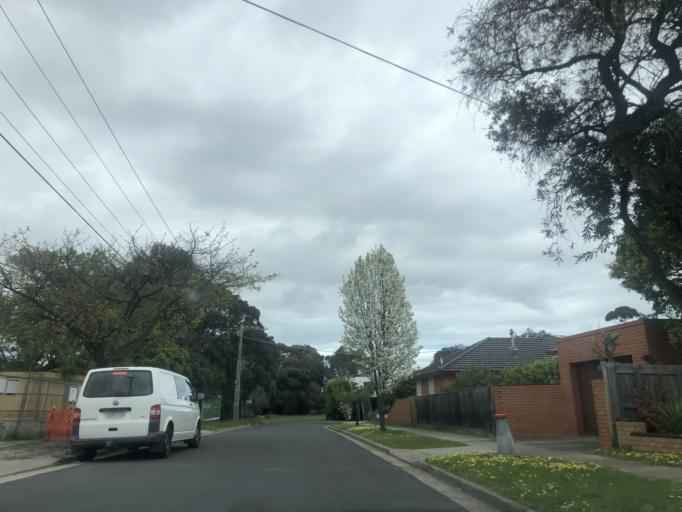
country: AU
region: Victoria
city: Clayton
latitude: -37.9205
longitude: 145.1064
